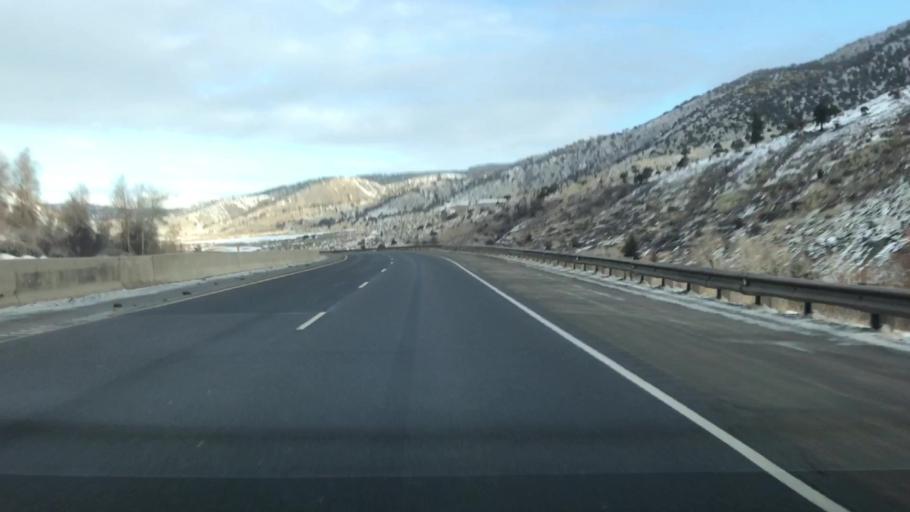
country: US
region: Colorado
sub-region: Eagle County
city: Edwards
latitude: 39.6779
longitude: -106.6478
